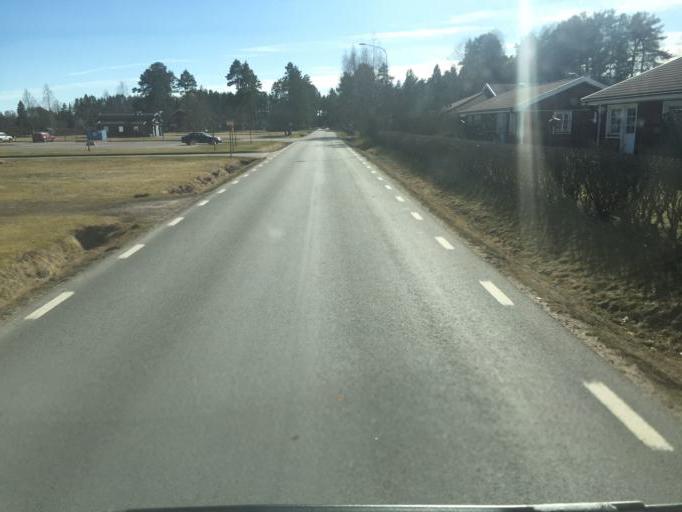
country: SE
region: Dalarna
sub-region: Vansbro Kommun
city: Vansbro
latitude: 60.4823
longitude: 14.0094
